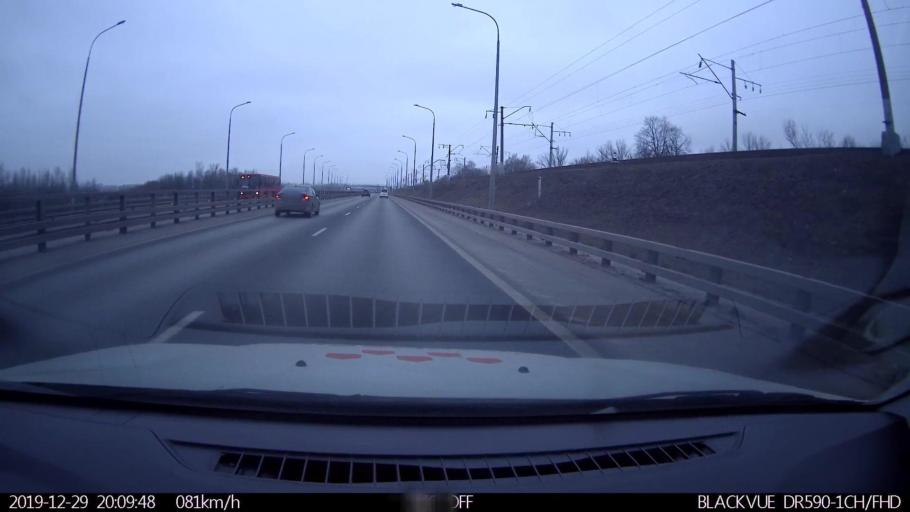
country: RU
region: Nizjnij Novgorod
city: Neklyudovo
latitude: 56.3718
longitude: 43.9460
